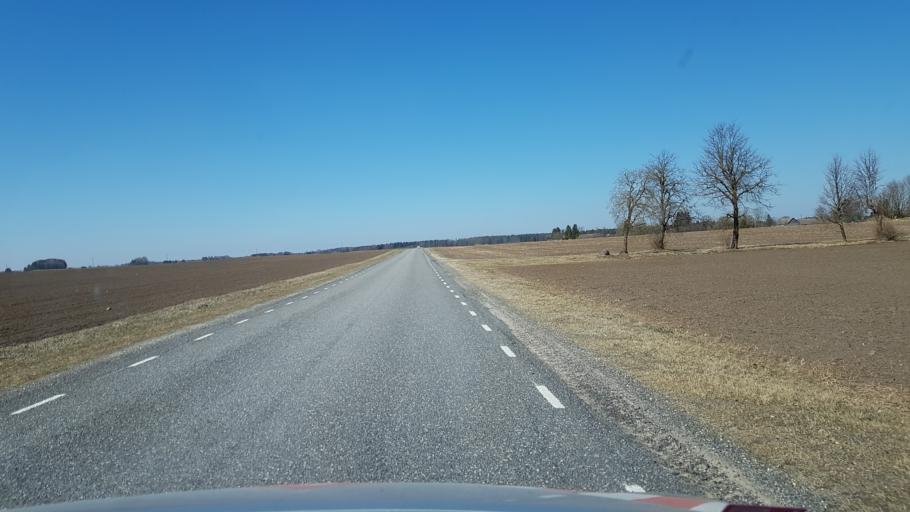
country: EE
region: Laeaene-Virumaa
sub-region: Rakke vald
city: Rakke
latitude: 59.0013
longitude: 26.1965
